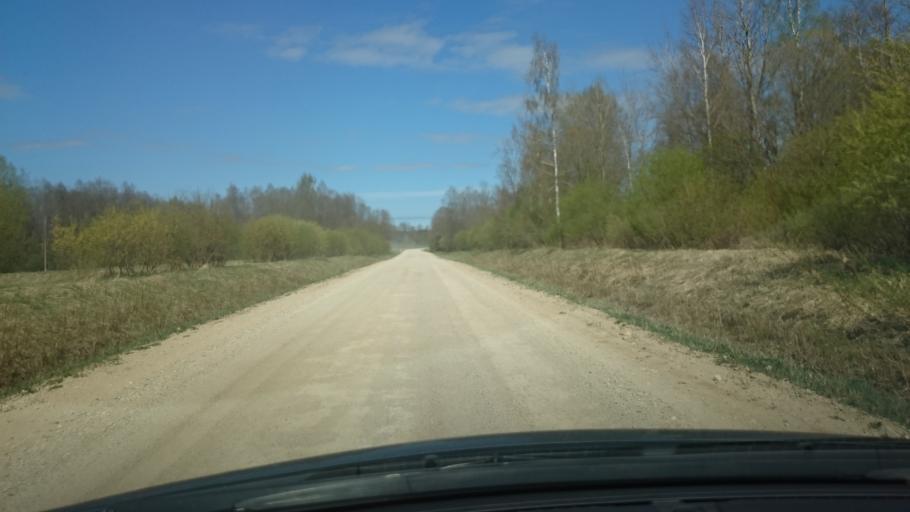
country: EE
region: Ida-Virumaa
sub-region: Sillamaee linn
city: Sillamae
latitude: 59.1083
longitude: 27.7965
